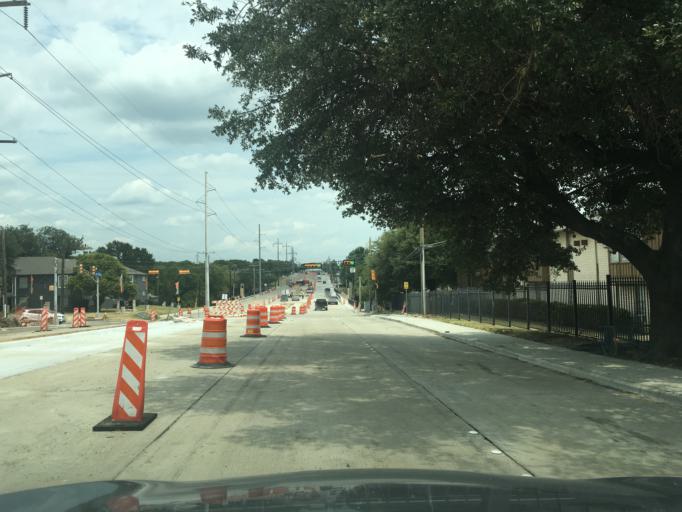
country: US
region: Texas
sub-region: Dallas County
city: Richardson
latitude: 32.9400
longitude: -96.7586
